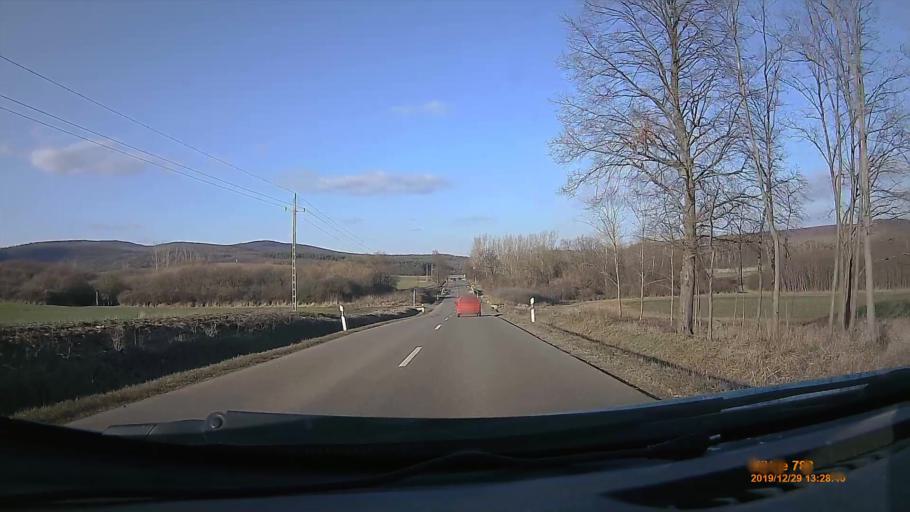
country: HU
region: Heves
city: Verpelet
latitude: 47.8649
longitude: 20.2020
